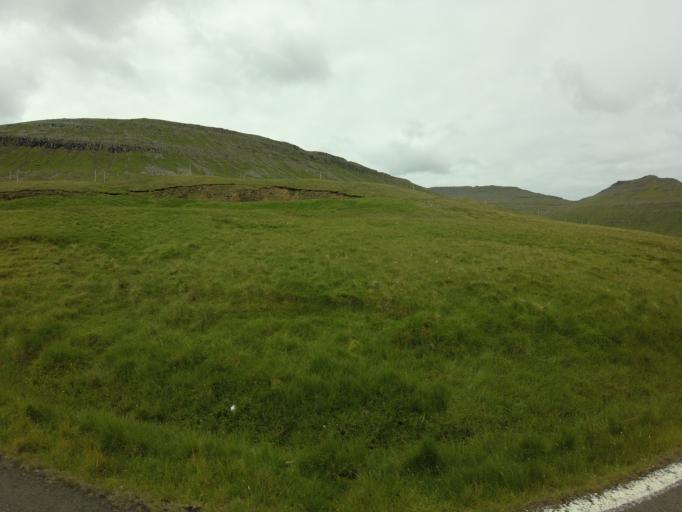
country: FO
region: Suduroy
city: Tvoroyri
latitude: 61.5304
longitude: -6.8355
